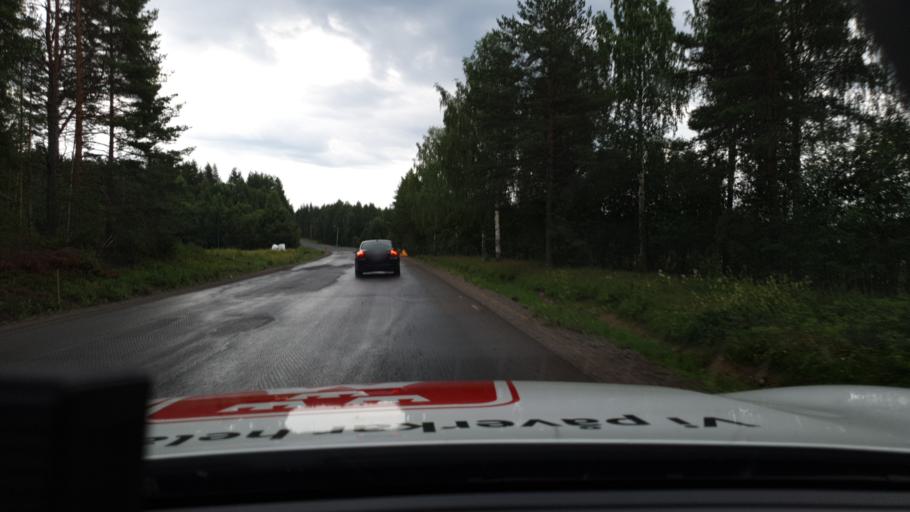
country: SE
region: Norrbotten
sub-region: Bodens Kommun
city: Boden
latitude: 65.8611
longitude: 21.4308
